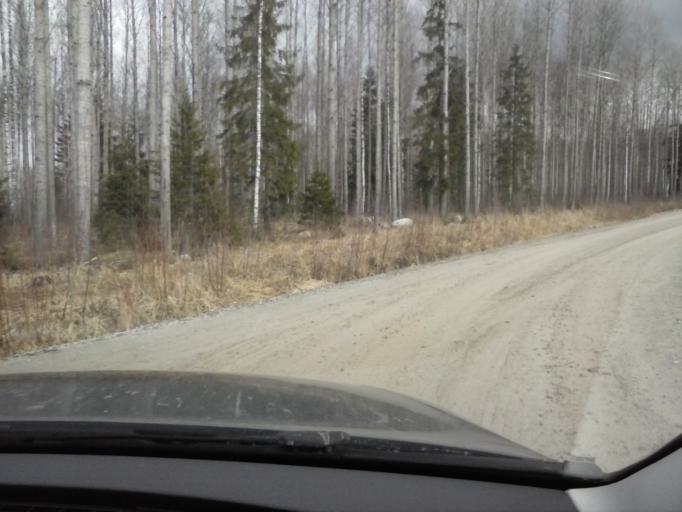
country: EE
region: Jogevamaa
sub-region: Mustvee linn
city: Mustvee
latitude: 59.0706
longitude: 26.8615
